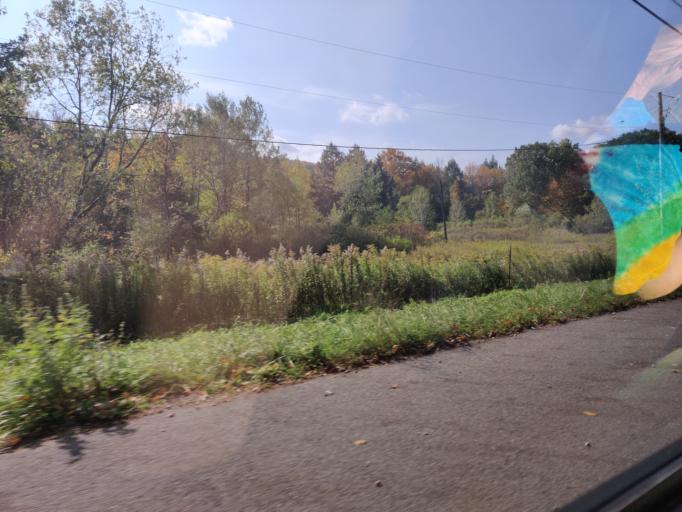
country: US
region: Pennsylvania
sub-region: Warren County
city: Warren
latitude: 41.8206
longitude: -79.1027
